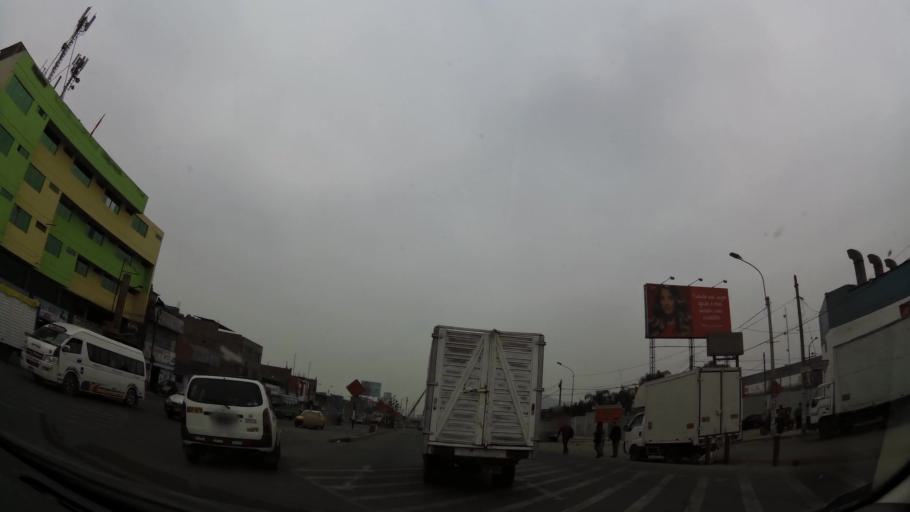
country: PE
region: Lima
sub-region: Lima
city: La Molina
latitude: -12.0528
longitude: -76.9590
